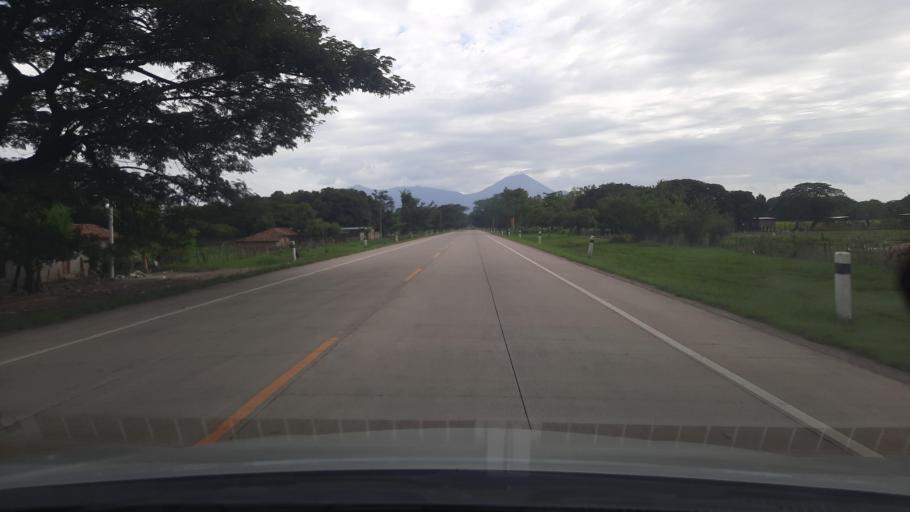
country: NI
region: Chinandega
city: Somotillo
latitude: 12.8554
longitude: -86.8711
